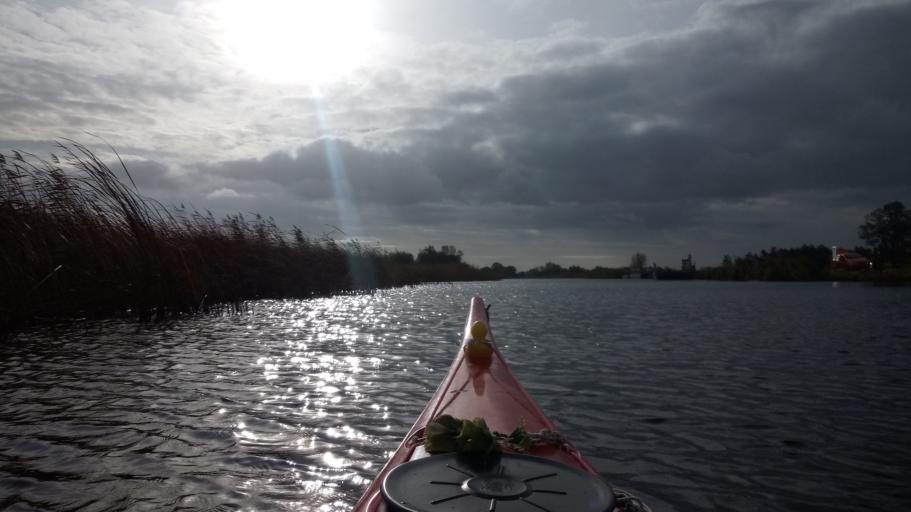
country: NL
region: Overijssel
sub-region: Gemeente Steenwijkerland
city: Sint Jansklooster
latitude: 52.6562
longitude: 6.0575
